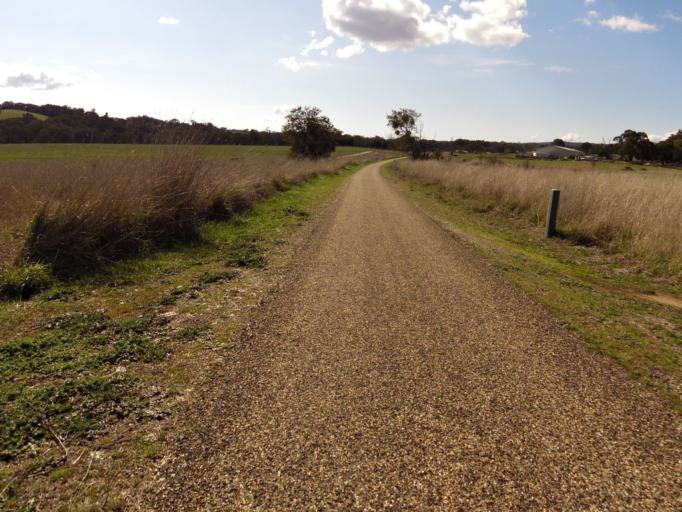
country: AU
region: Victoria
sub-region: Wangaratta
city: Wangaratta
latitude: -36.3964
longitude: 146.6537
